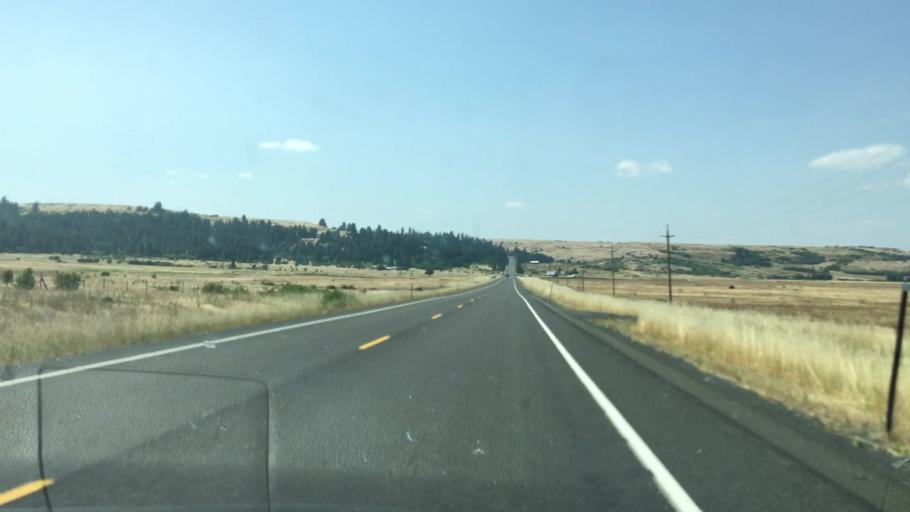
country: US
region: Idaho
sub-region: Idaho County
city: Grangeville
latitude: 45.8859
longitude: -116.2056
